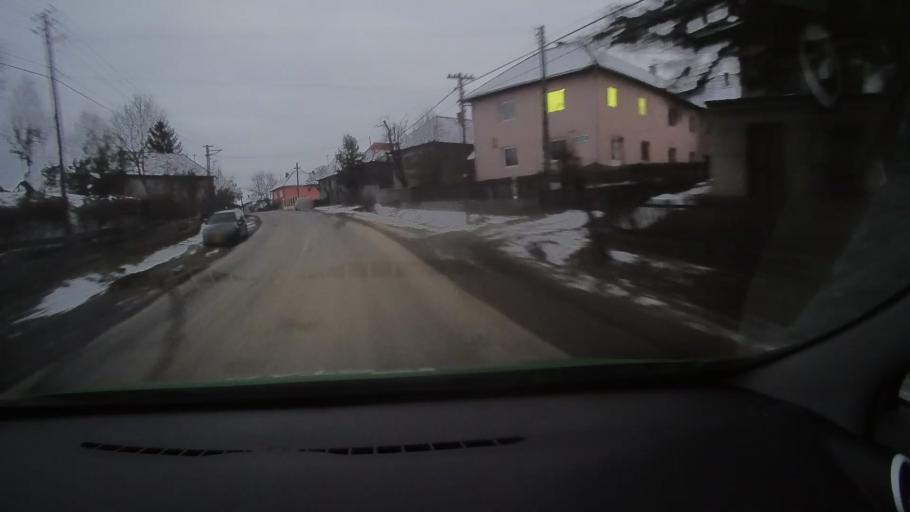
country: RO
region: Harghita
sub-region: Comuna Darjiu
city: Darjiu
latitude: 46.2124
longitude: 25.2398
